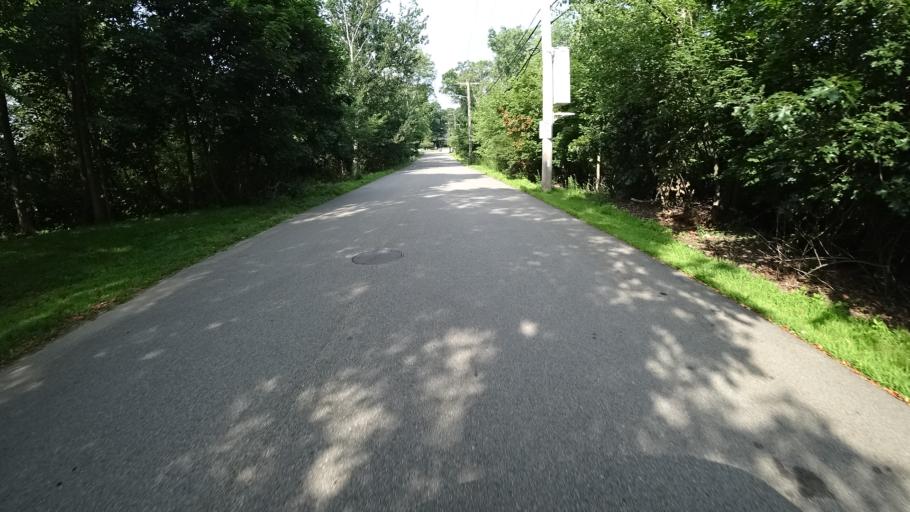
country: US
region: Massachusetts
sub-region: Norfolk County
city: Dedham
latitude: 42.2412
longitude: -71.1692
